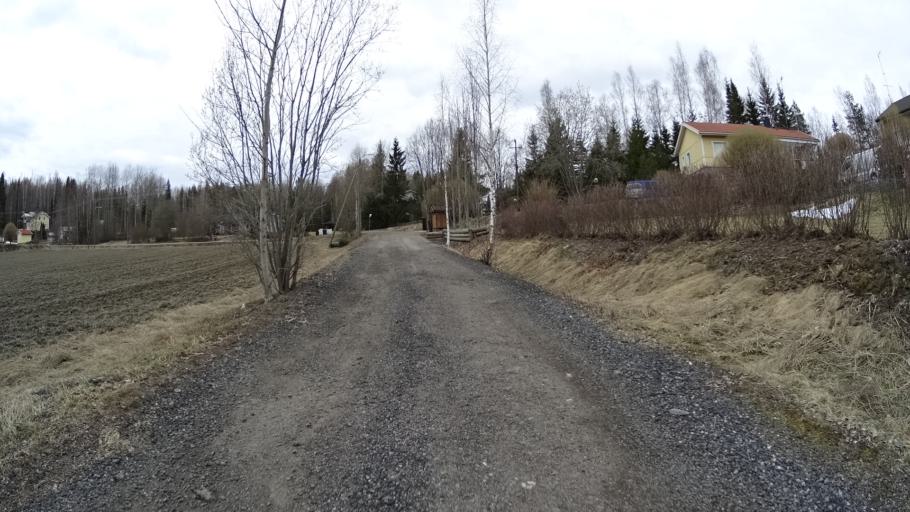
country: FI
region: Uusimaa
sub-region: Helsinki
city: Kilo
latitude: 60.2977
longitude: 24.7888
